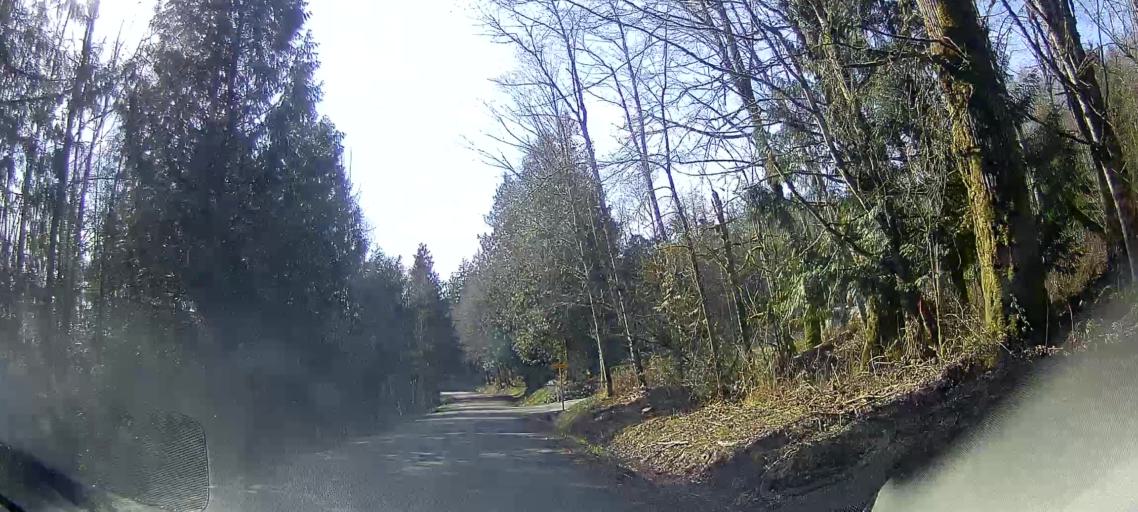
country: US
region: Washington
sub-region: Skagit County
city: Burlington
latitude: 48.5891
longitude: -122.3837
